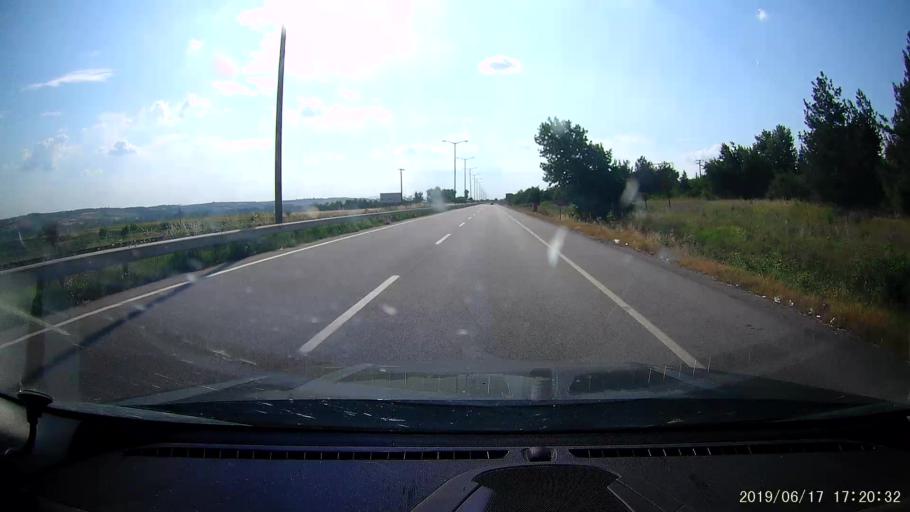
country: GR
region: East Macedonia and Thrace
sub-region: Nomos Evrou
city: Rizia
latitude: 41.7022
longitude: 26.4125
